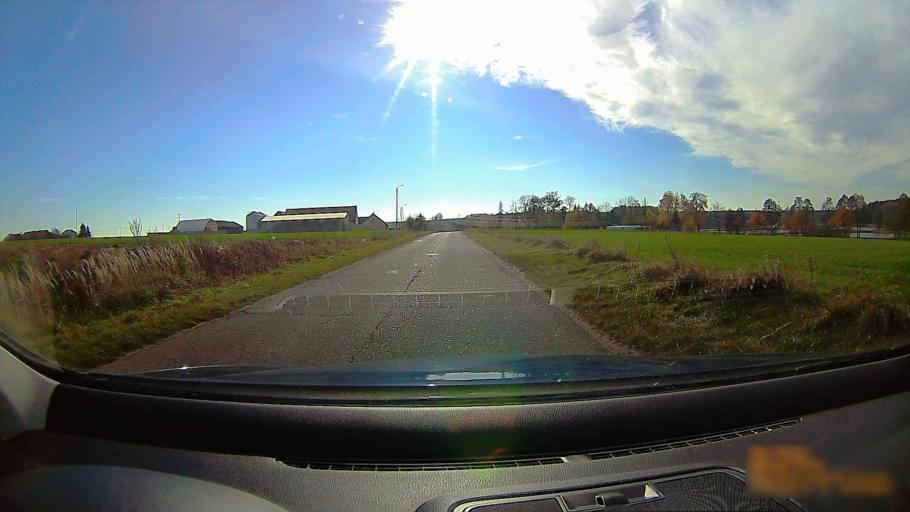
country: PL
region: Greater Poland Voivodeship
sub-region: Powiat ostrzeszowski
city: Doruchow
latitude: 51.3973
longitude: 18.0303
